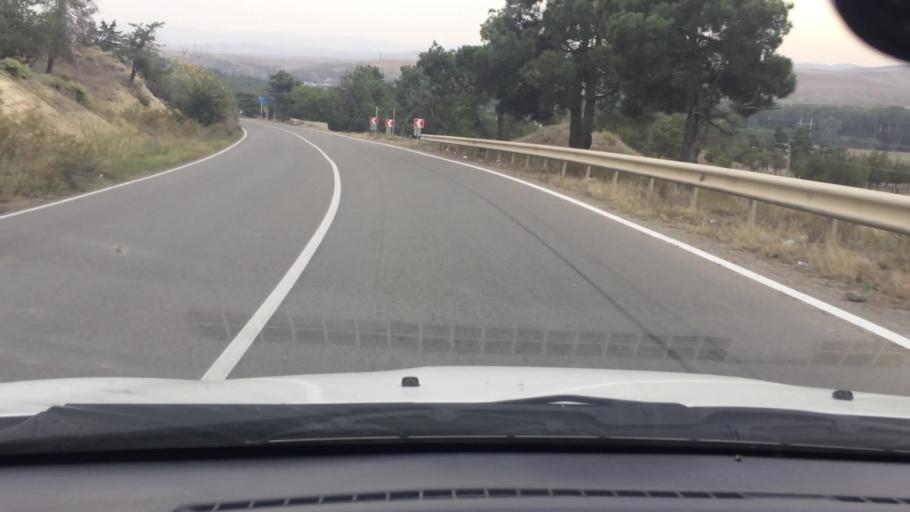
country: GE
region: Kvemo Kartli
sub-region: Gardabani
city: Gardabani
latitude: 41.3447
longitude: 45.0681
